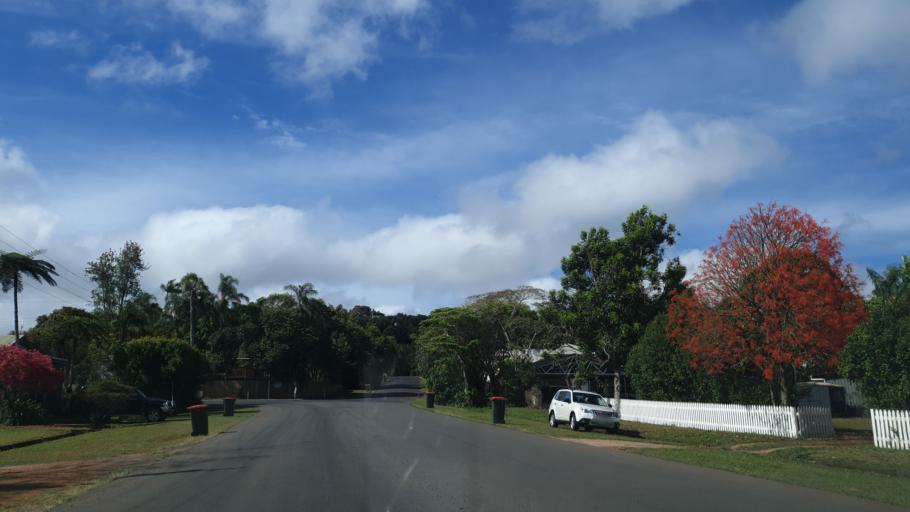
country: AU
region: Queensland
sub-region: Tablelands
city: Atherton
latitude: -17.3521
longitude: 145.5913
